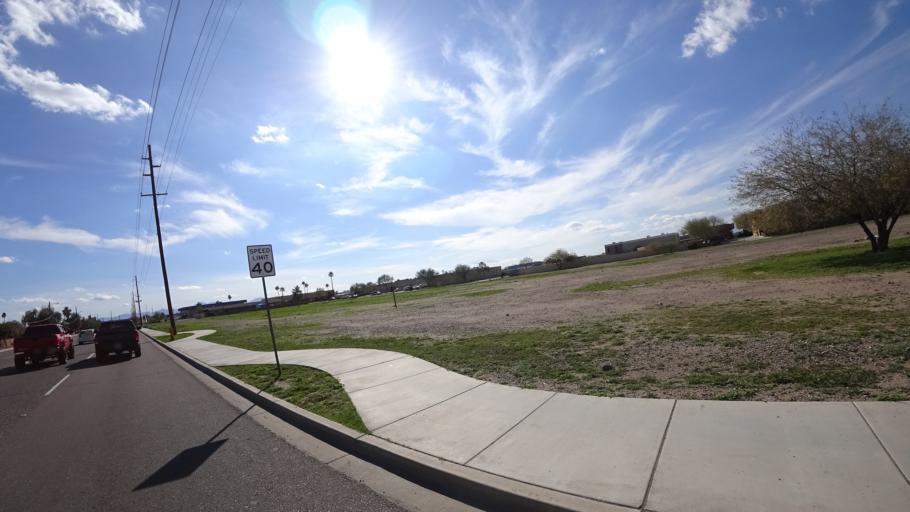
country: US
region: Arizona
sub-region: Maricopa County
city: Peoria
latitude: 33.5737
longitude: -112.2204
